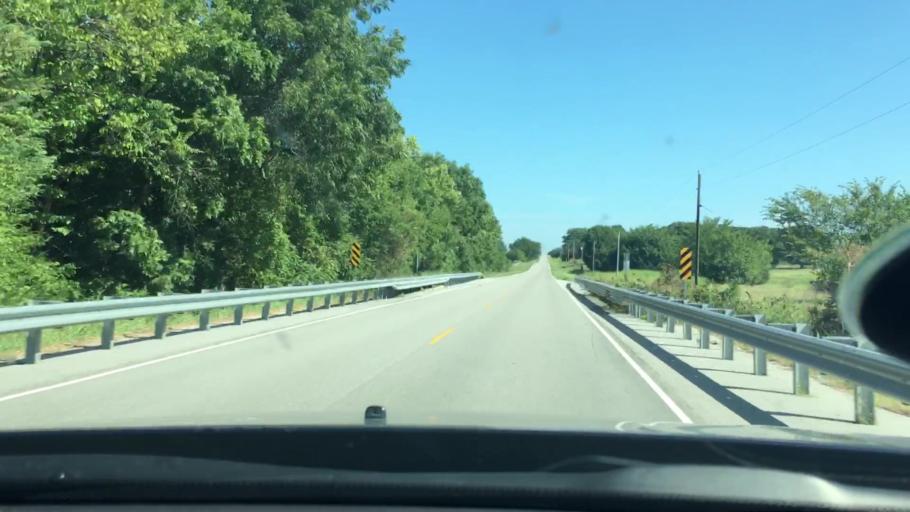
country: US
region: Oklahoma
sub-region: Johnston County
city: Tishomingo
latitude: 34.2882
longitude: -96.5487
